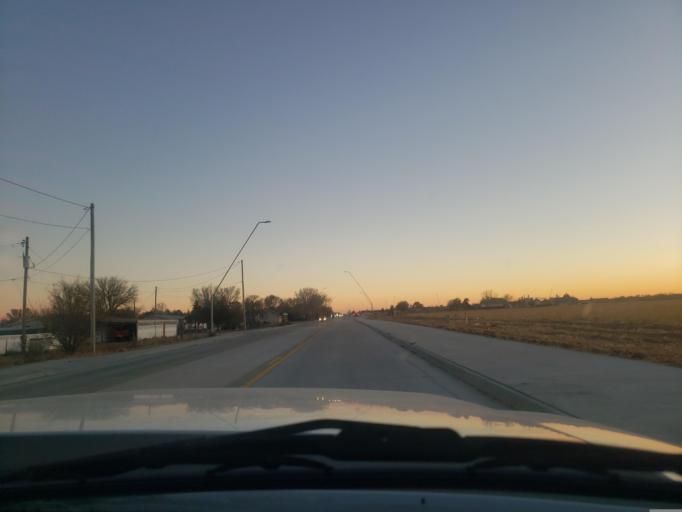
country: US
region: Kansas
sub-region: Finney County
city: Garden City
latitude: 37.9778
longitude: -100.8290
